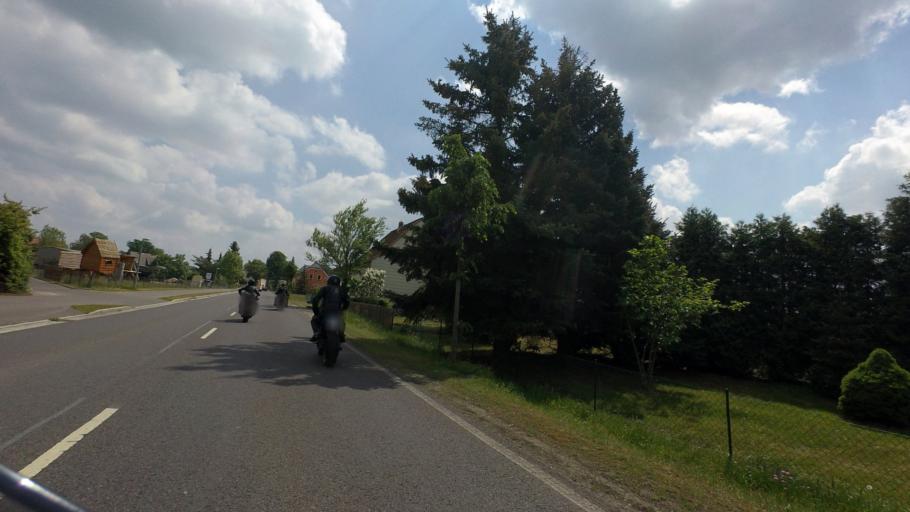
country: DE
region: Saxony
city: Weisskeissel
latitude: 51.4959
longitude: 14.7173
